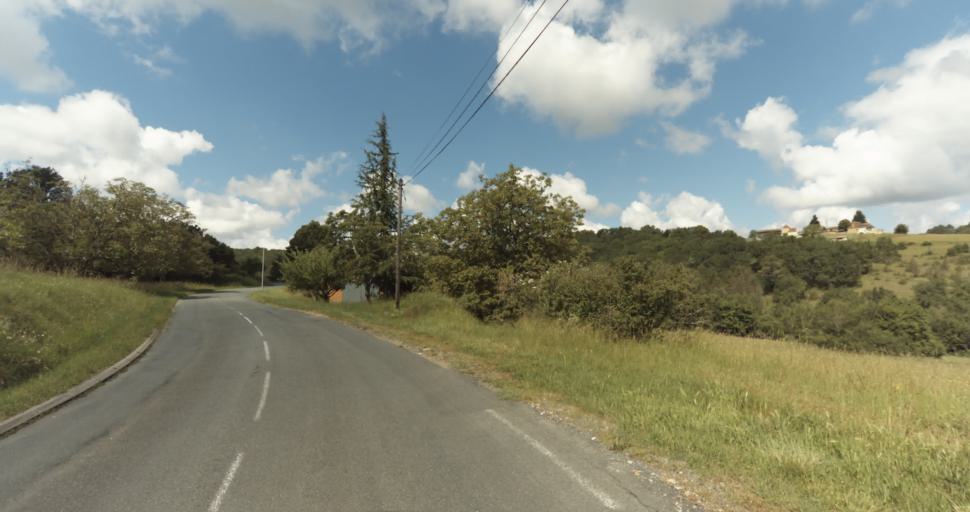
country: FR
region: Aquitaine
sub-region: Departement de la Dordogne
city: Le Bugue
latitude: 44.8263
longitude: 0.8902
